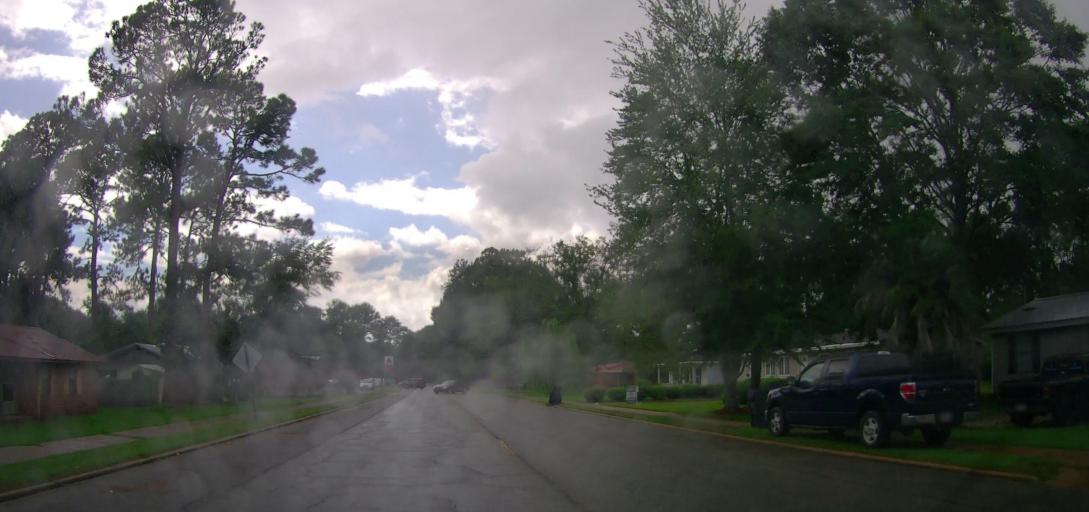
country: US
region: Georgia
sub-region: Ben Hill County
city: Fitzgerald
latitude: 31.7148
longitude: -83.2681
